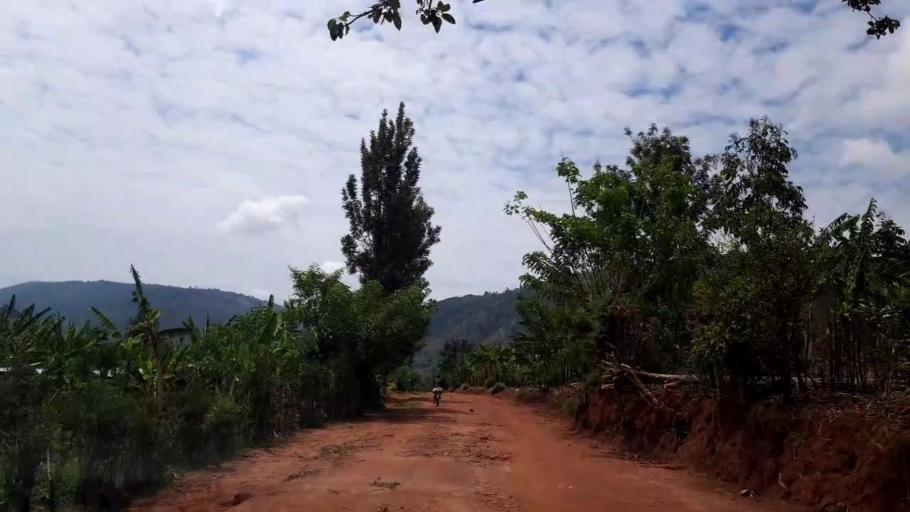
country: RW
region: Northern Province
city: Byumba
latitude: -1.4936
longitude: 30.1955
